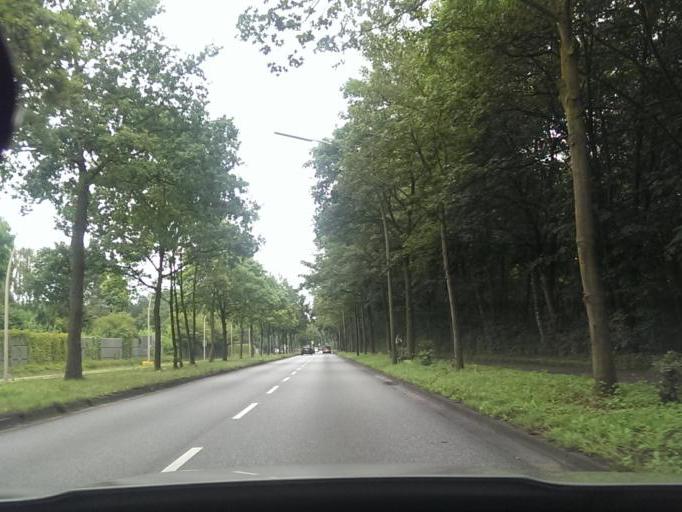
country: DE
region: Hamburg
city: Hummelsbuettel
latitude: 53.6475
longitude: 10.0430
